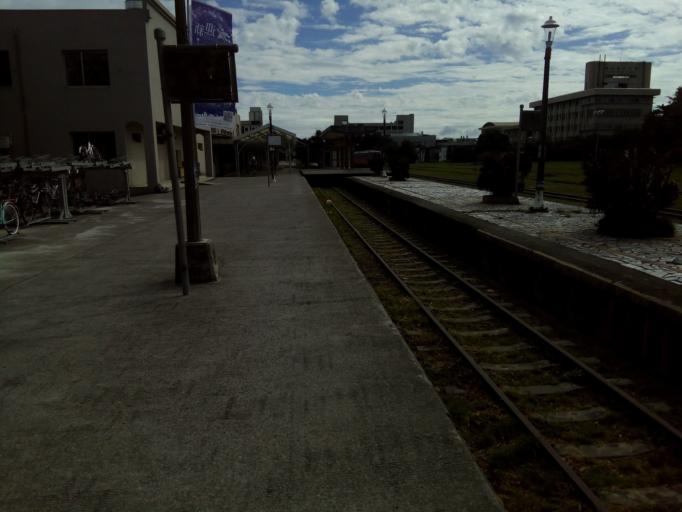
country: TW
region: Taiwan
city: Taitung City
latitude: 22.7523
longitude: 121.1466
